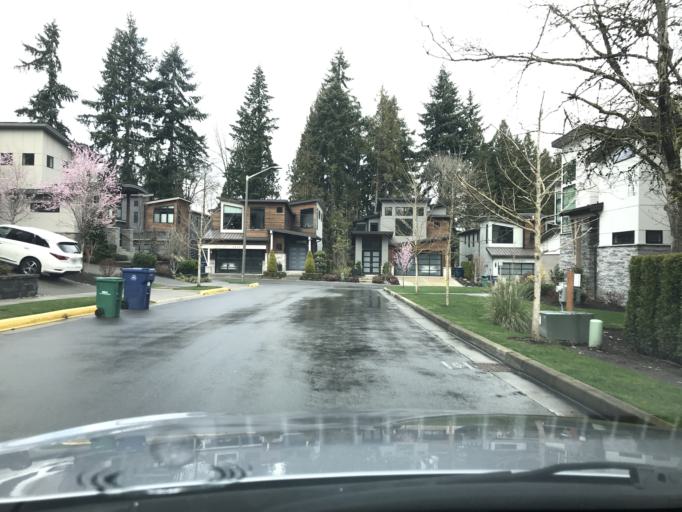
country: US
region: Washington
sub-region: King County
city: Redmond
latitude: 47.6558
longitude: -122.1266
